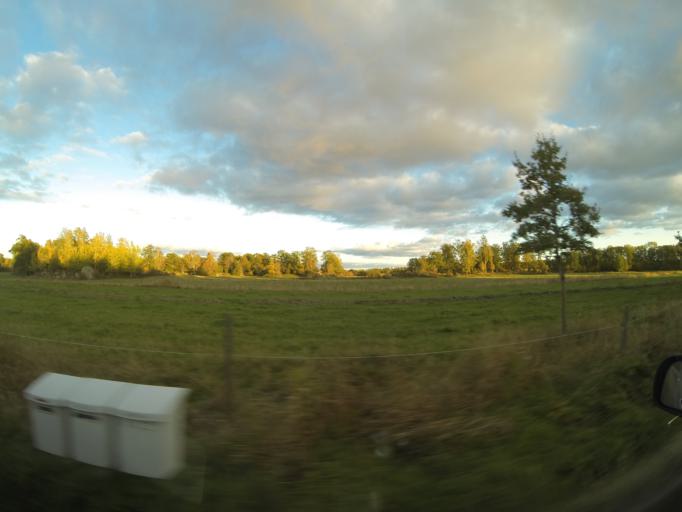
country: SE
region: Soedermanland
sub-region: Eskilstuna Kommun
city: Kvicksund
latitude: 59.4889
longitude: 16.3331
